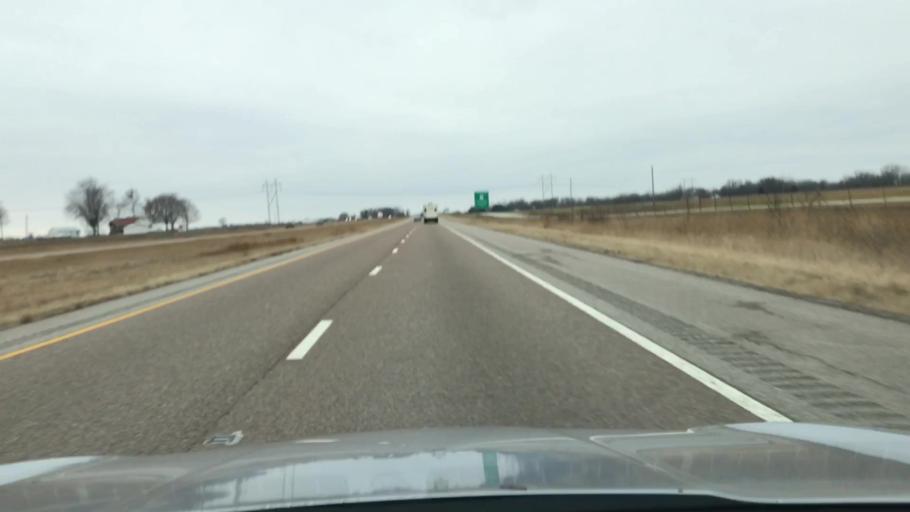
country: US
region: Illinois
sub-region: Madison County
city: Worden
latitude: 38.9467
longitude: -89.7815
